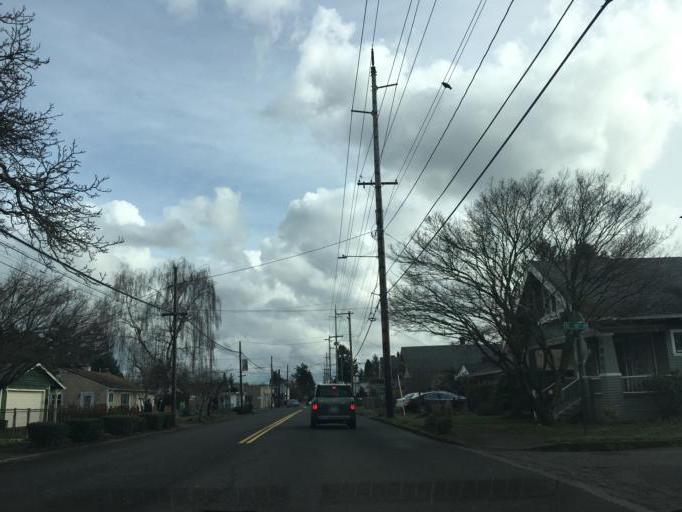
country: US
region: Oregon
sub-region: Multnomah County
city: Lents
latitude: 45.4903
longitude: -122.6112
